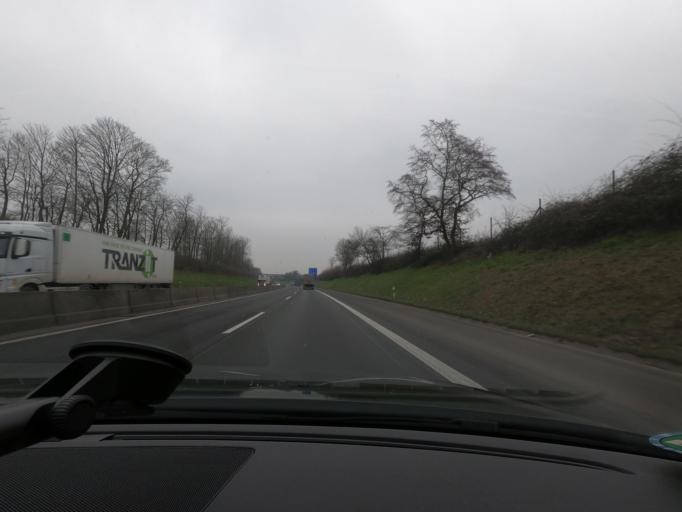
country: DE
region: North Rhine-Westphalia
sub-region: Regierungsbezirk Dusseldorf
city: Nettetal
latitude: 51.3207
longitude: 6.2227
